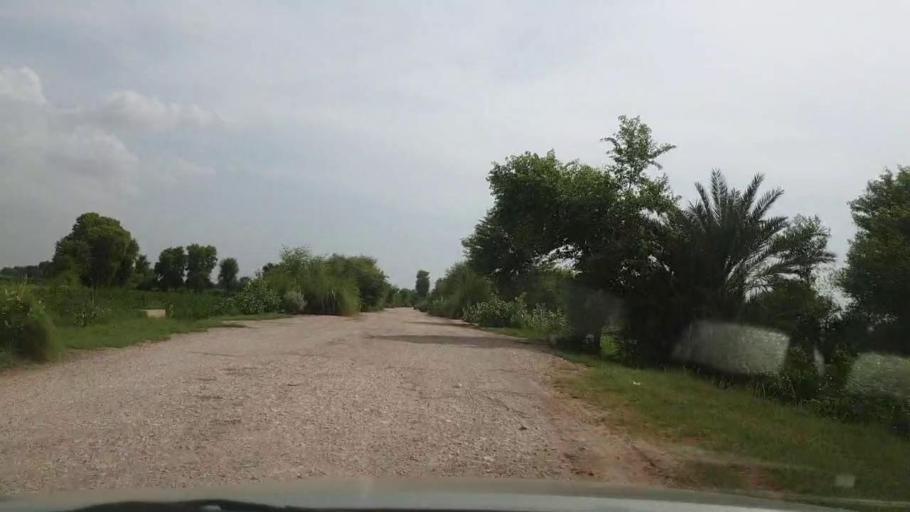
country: PK
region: Sindh
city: Kot Diji
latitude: 27.1169
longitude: 69.0243
